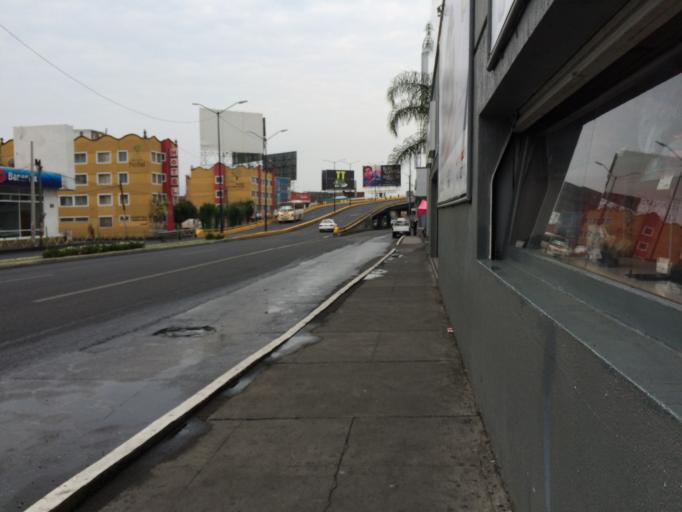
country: MX
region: Michoacan
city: Morelia
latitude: 19.7021
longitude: -101.2111
